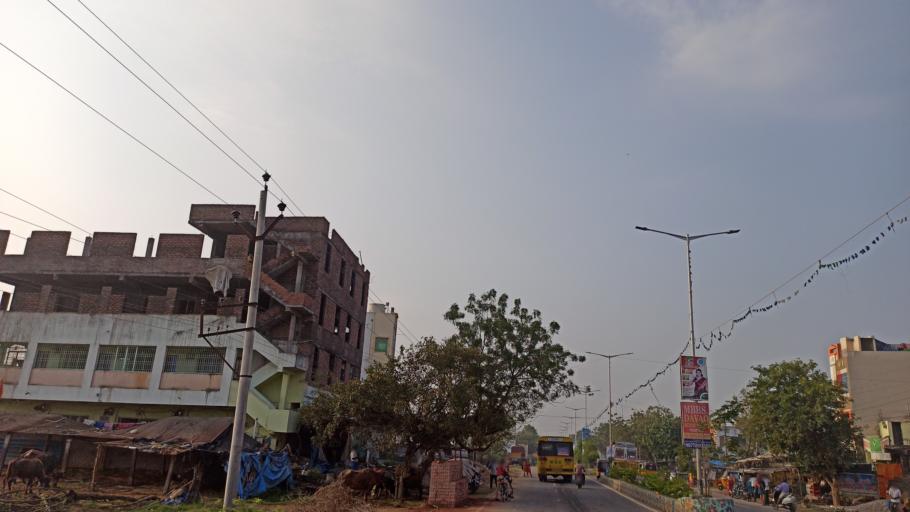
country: IN
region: Andhra Pradesh
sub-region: Guntur
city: Narasaraopet
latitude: 16.2515
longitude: 80.0575
